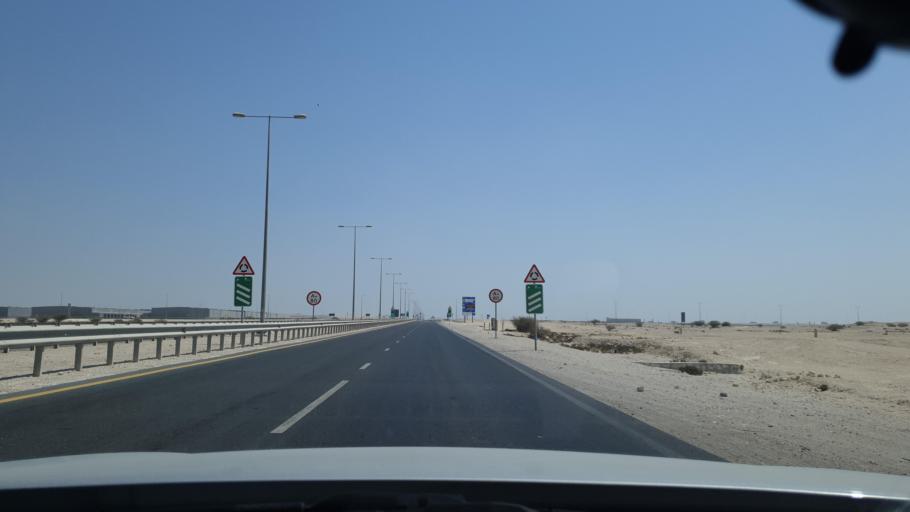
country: QA
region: Baladiyat Umm Salal
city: Umm Salal Muhammad
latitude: 25.3879
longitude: 51.3453
